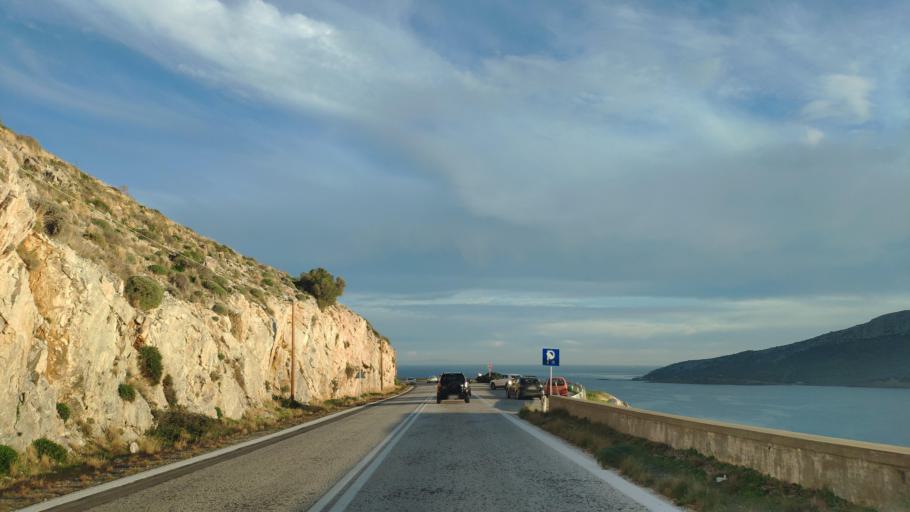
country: GR
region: Attica
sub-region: Nomarchia Anatolikis Attikis
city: Palaia Fokaia
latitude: 37.6721
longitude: 23.9398
